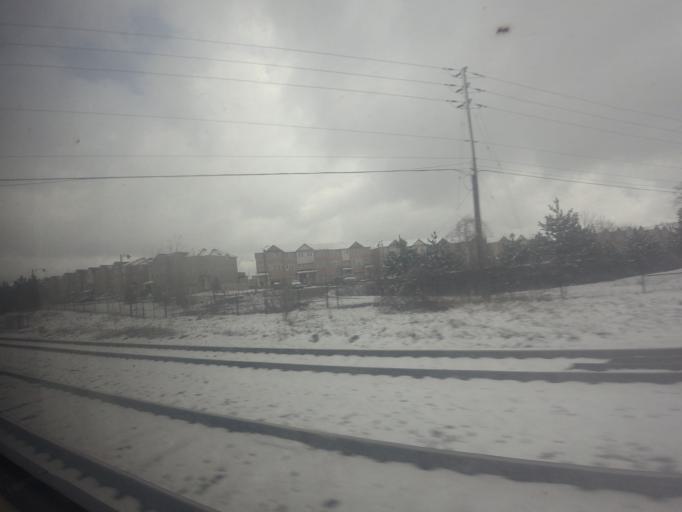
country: CA
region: Ontario
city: Scarborough
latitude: 43.7208
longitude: -79.2524
